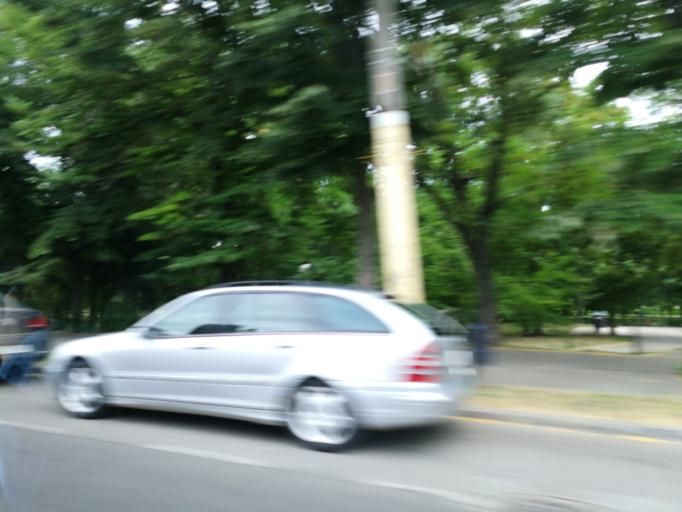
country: RO
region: Constanta
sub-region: Municipiul Constanta
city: Constanta
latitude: 44.2101
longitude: 28.6289
